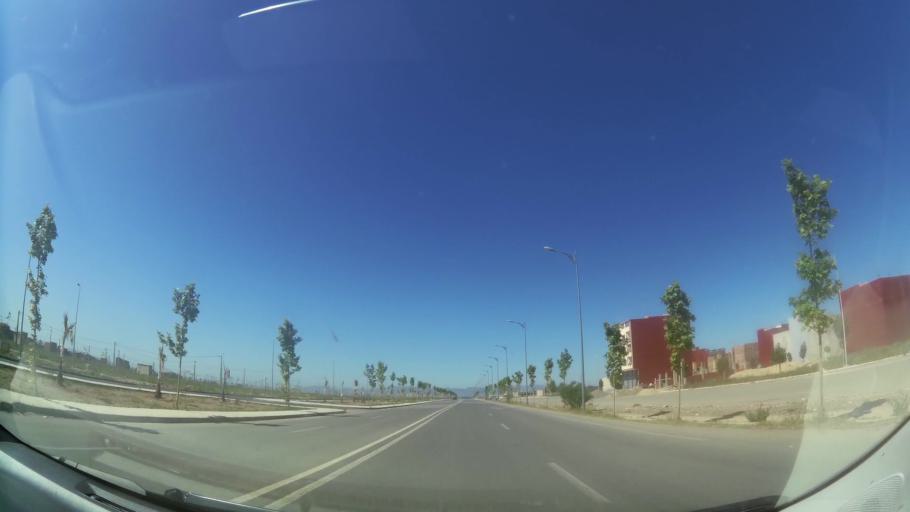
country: MA
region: Oriental
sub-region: Oujda-Angad
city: Oujda
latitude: 34.6800
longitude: -1.8591
